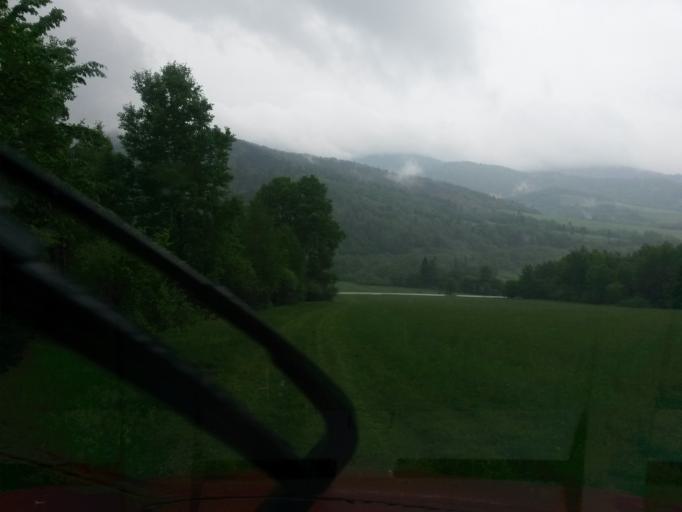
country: SK
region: Kosicky
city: Medzev
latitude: 48.7878
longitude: 20.7750
